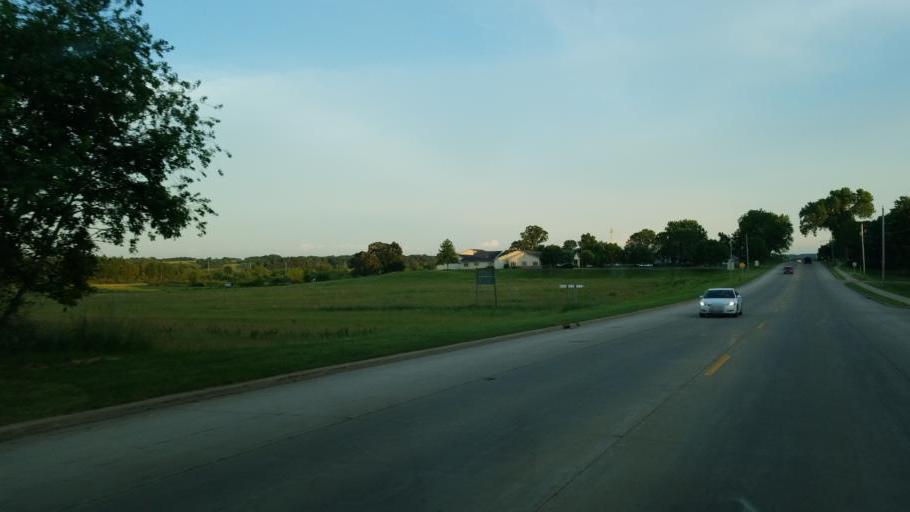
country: US
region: Wisconsin
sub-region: Monroe County
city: Tomah
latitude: 43.9675
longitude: -90.5049
